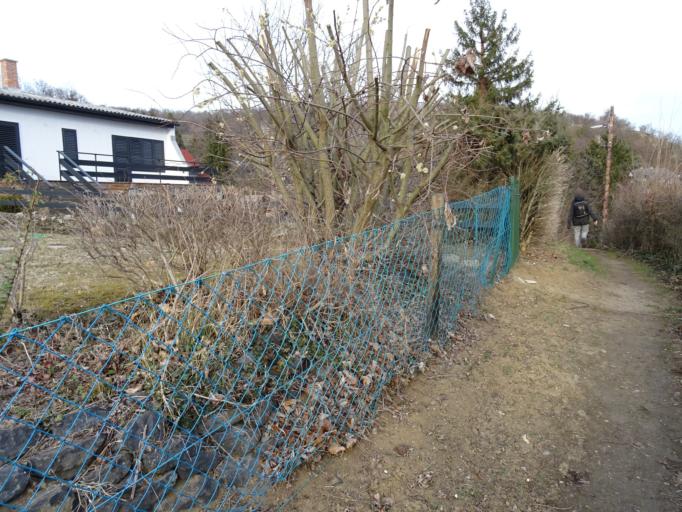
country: HU
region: Veszprem
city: Badacsonytomaj
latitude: 46.7909
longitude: 17.4354
